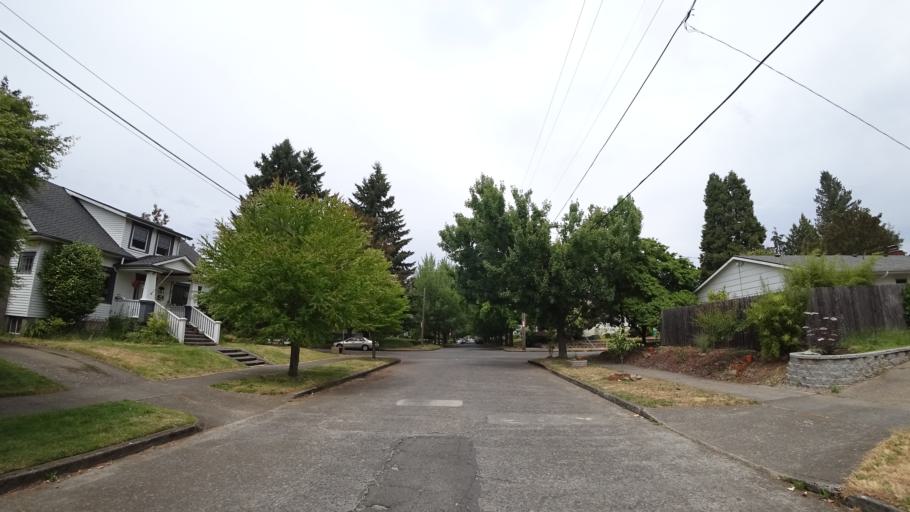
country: US
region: Oregon
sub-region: Multnomah County
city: Portland
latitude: 45.5678
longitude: -122.6976
